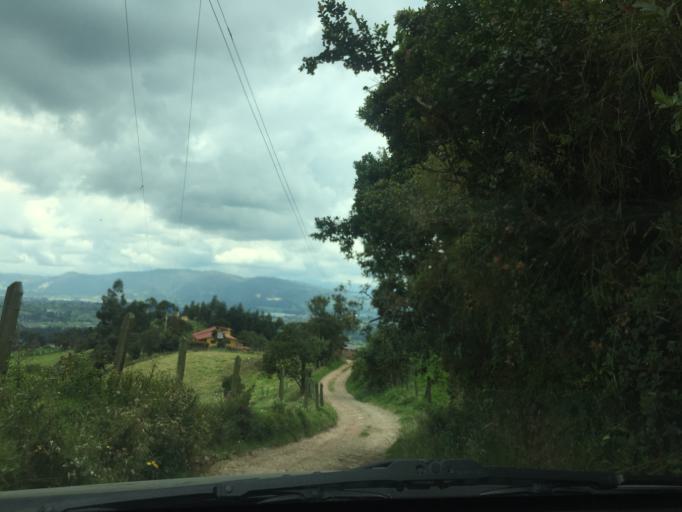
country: CO
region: Cundinamarca
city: Zipaquira
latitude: 5.0548
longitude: -74.0139
